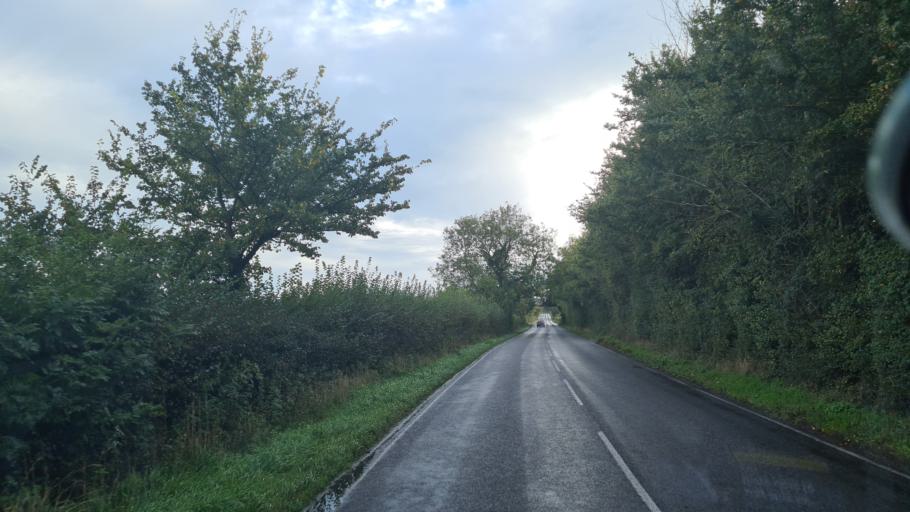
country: GB
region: England
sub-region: West Sussex
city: Arundel
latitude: 50.8446
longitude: -0.5703
